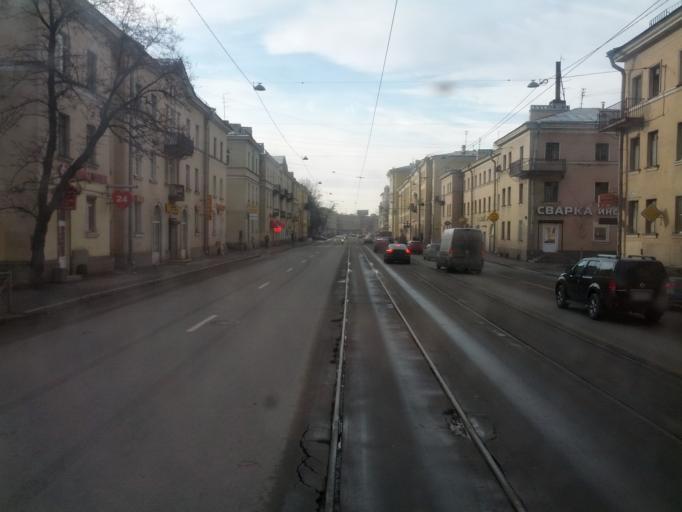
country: RU
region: Leningrad
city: Kalininskiy
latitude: 59.9506
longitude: 30.4147
